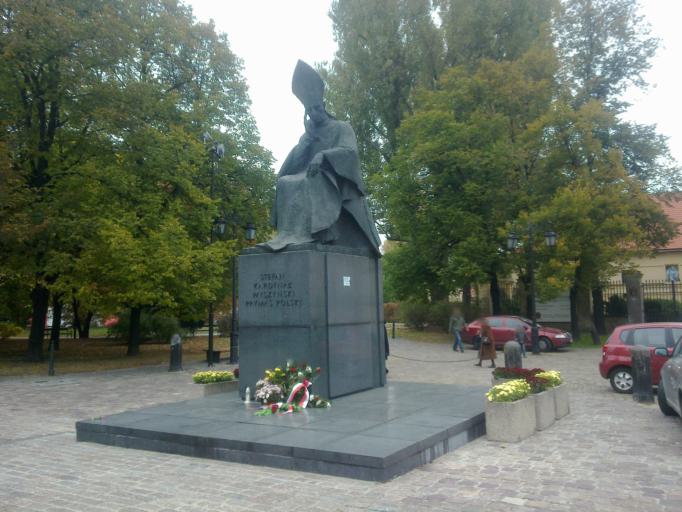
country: PL
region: Masovian Voivodeship
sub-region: Warszawa
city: Srodmiescie
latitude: 52.2409
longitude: 21.0166
